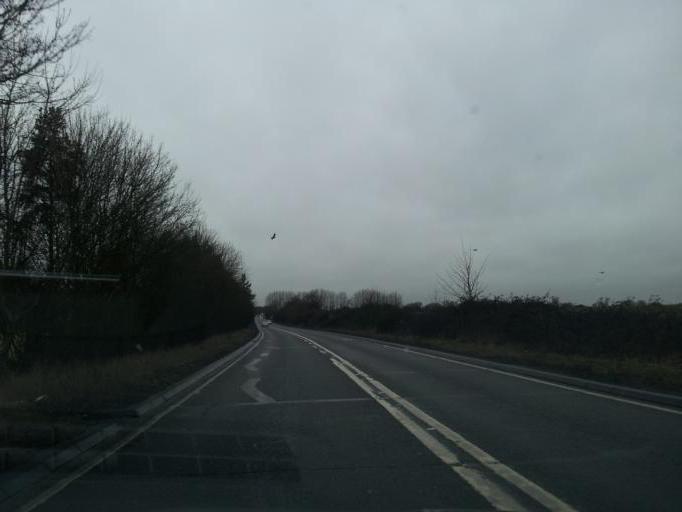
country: GB
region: England
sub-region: Essex
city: Mistley
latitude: 51.9128
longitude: 1.1372
